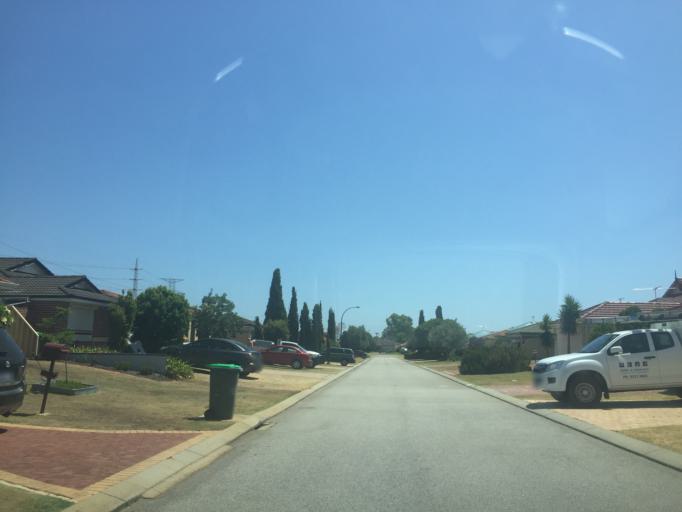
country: AU
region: Western Australia
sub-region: City of Cockburn
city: City of Cockburn
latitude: -32.0943
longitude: 115.8430
